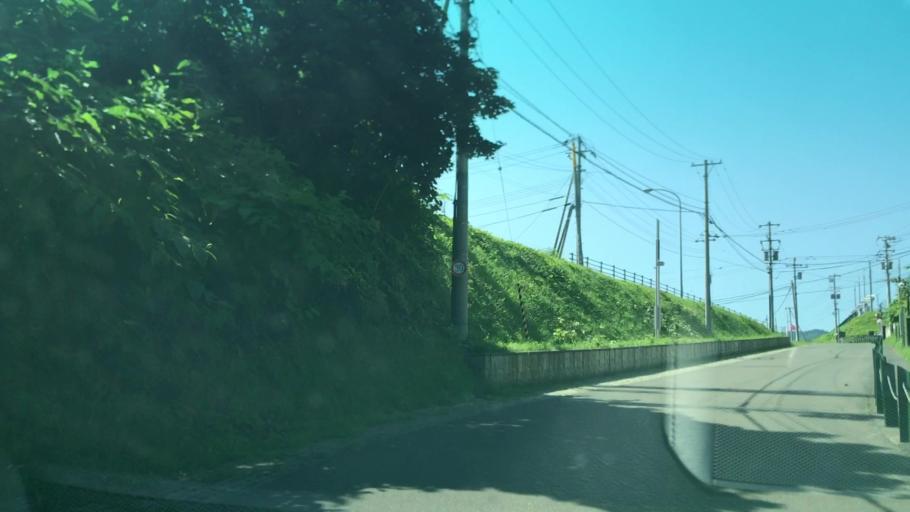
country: JP
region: Hokkaido
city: Iwanai
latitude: 43.1436
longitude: 140.4259
